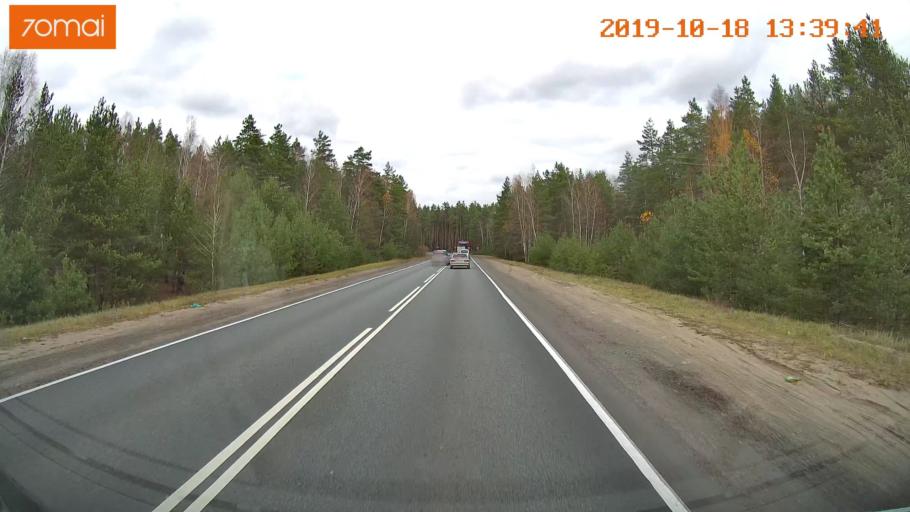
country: RU
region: Rjazan
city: Solotcha
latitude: 54.9017
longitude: 40.0029
